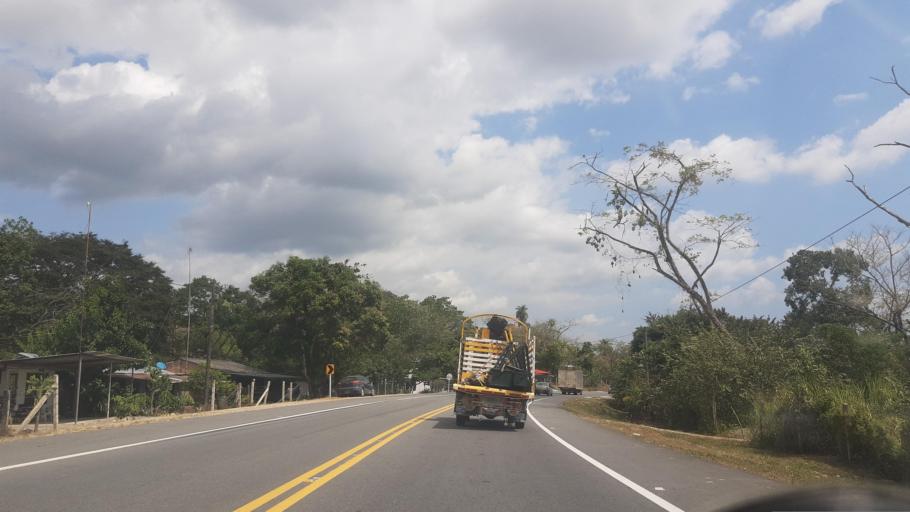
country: CO
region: Casanare
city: Tauramena
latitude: 5.0198
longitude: -72.6660
